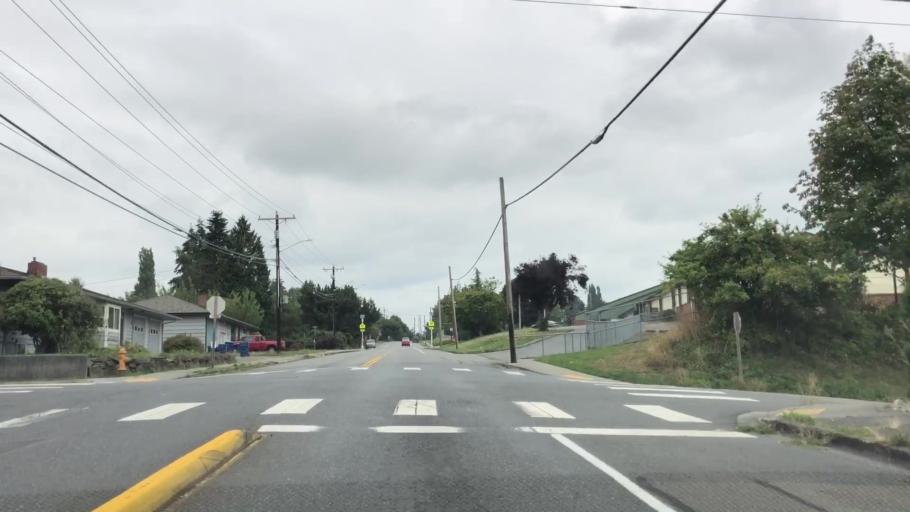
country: US
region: Washington
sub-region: Snohomish County
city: Snohomish
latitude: 47.9239
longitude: -122.0854
